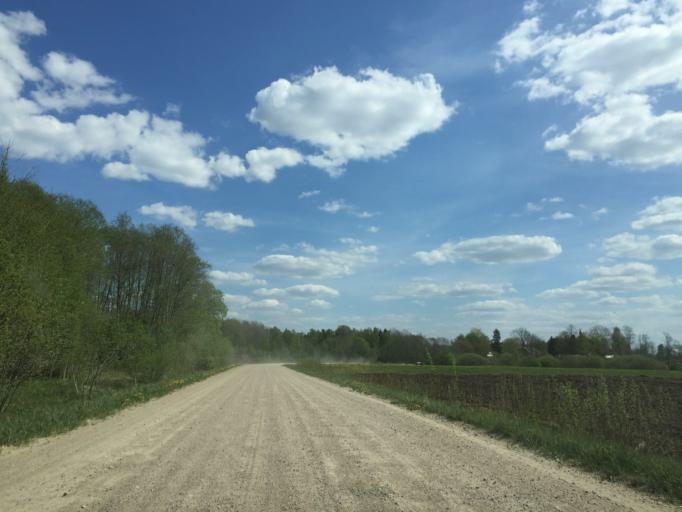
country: LV
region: Limbazu Rajons
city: Limbazi
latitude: 57.3941
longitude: 24.6449
